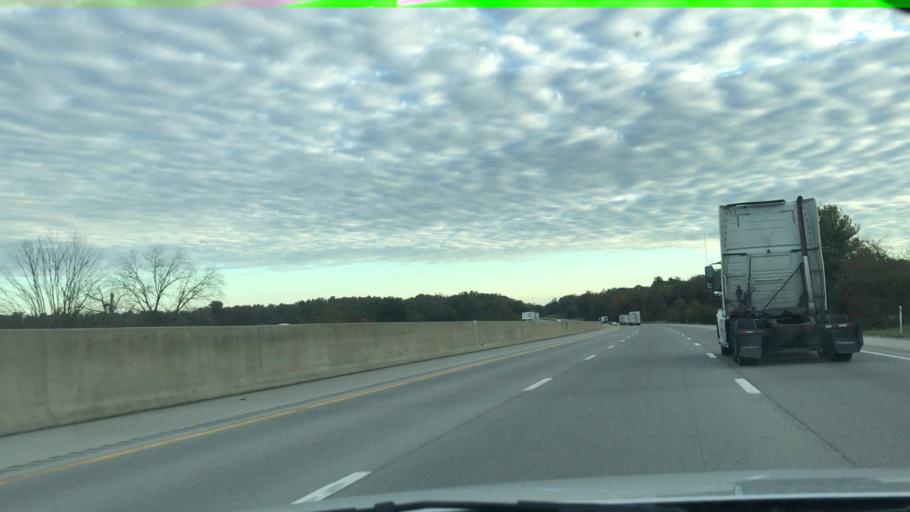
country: US
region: Kentucky
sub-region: Simpson County
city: Franklin
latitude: 36.7439
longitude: -86.4974
